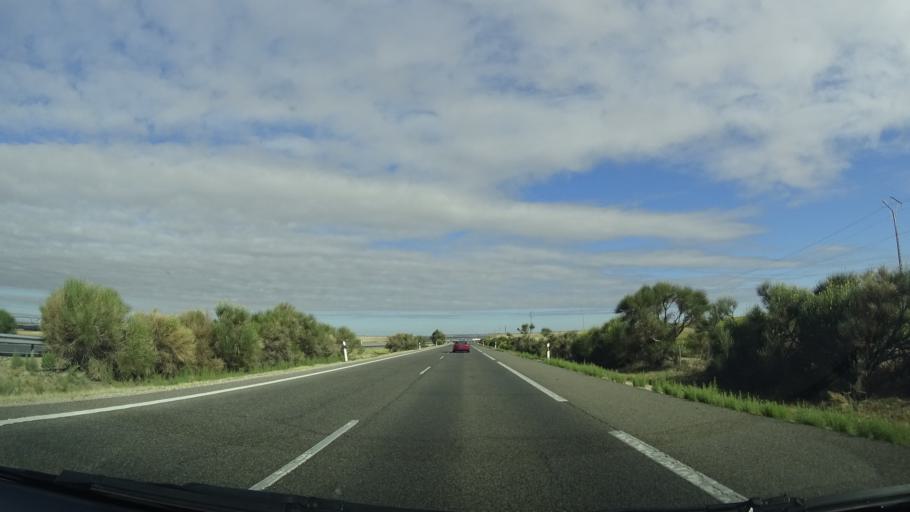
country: ES
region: Castille and Leon
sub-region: Provincia de Valladolid
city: San Vicente del Palacio
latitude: 41.2045
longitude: -4.8265
